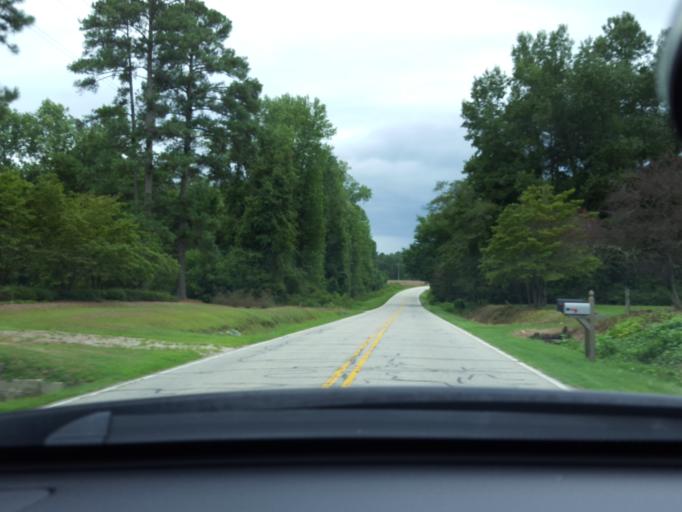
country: US
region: North Carolina
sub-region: Duplin County
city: Rose Hill
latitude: 34.8139
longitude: -78.1843
